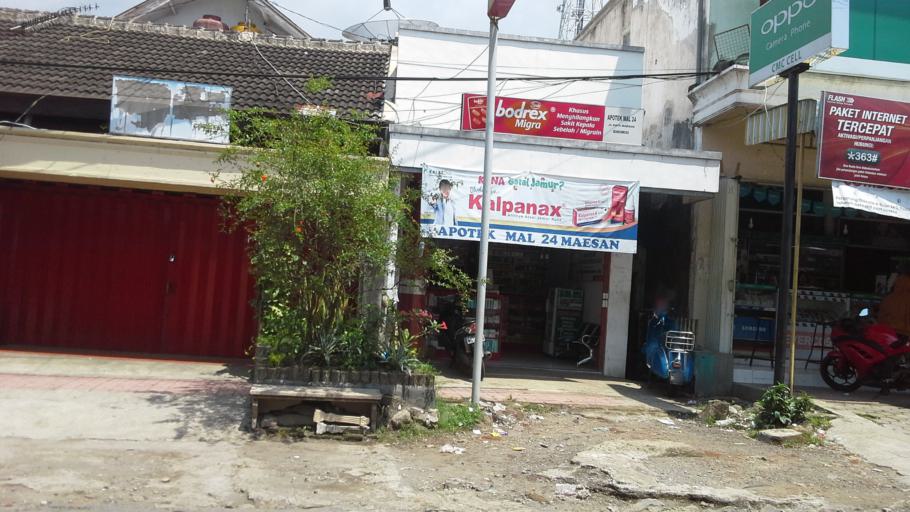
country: ID
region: East Java
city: Krajan Dua Sumbersari
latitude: -8.0300
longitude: 113.7764
